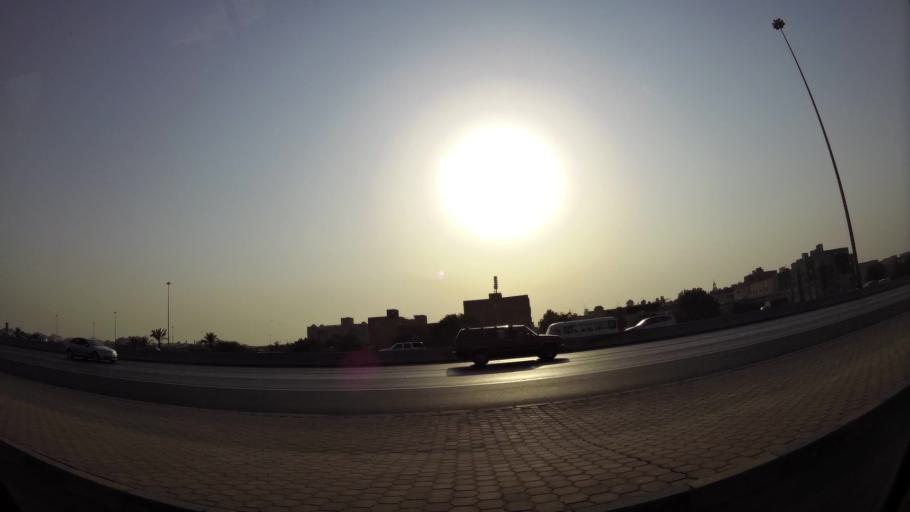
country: KW
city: Bayan
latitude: 29.3167
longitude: 48.0513
